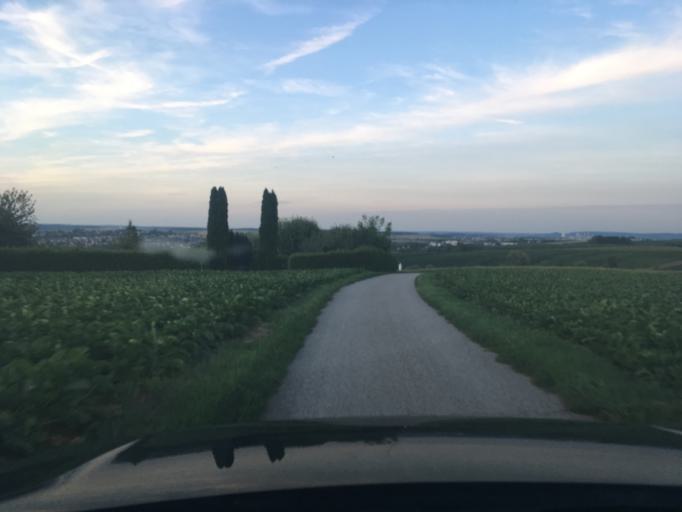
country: DE
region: Baden-Wuerttemberg
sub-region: Regierungsbezirk Stuttgart
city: Schwaigern
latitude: 49.1247
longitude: 9.0418
